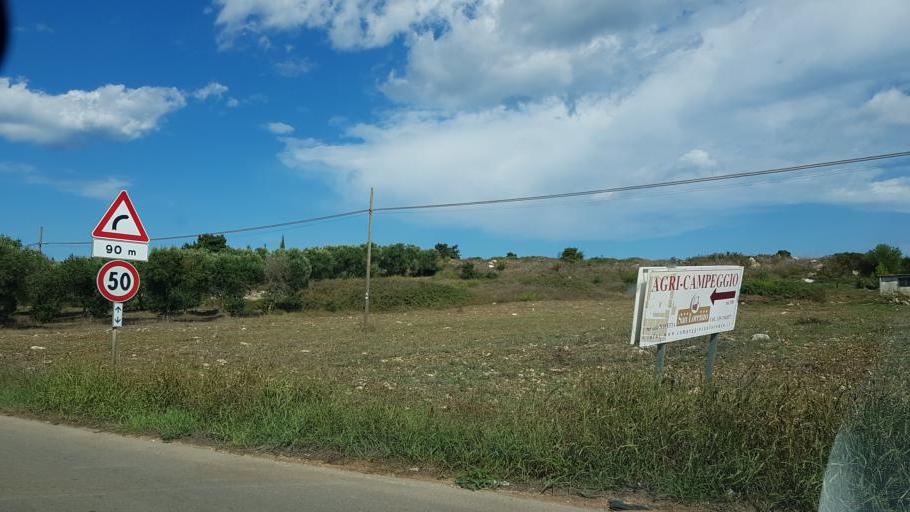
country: IT
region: Apulia
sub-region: Provincia di Lecce
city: Borgagne
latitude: 40.2228
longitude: 18.4416
